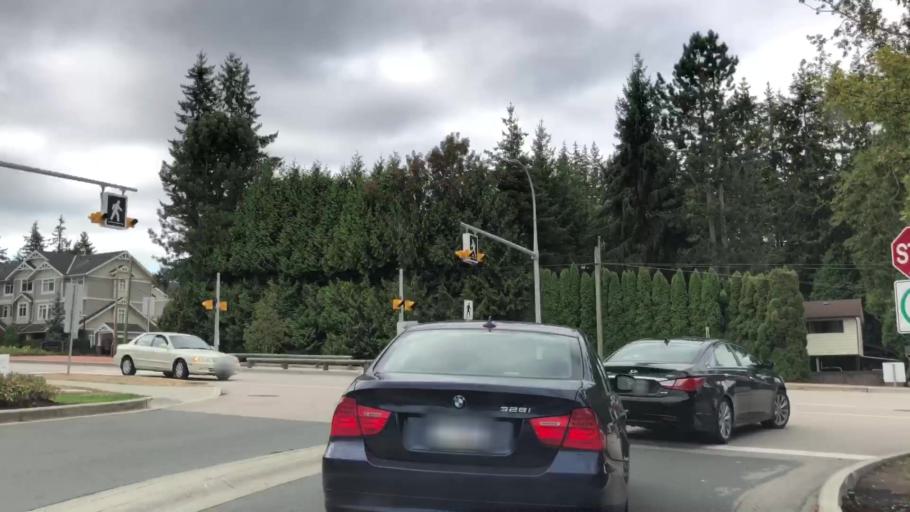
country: CA
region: British Columbia
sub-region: Greater Vancouver Regional District
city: White Rock
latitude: 49.0559
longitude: -122.8057
